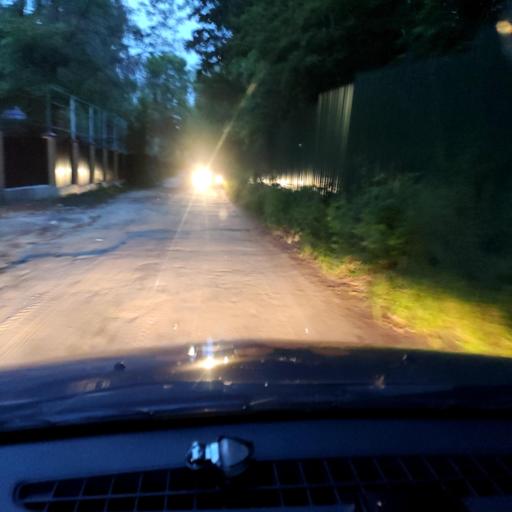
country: RU
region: Voronezj
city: Ramon'
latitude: 51.8291
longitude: 39.2784
